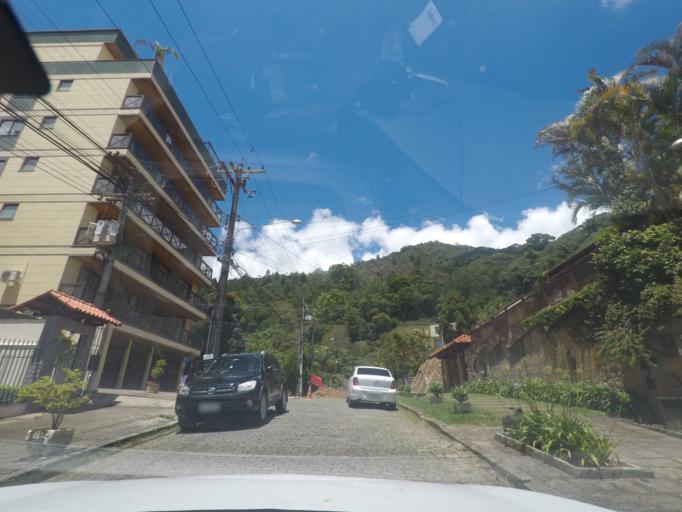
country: BR
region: Rio de Janeiro
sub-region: Teresopolis
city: Teresopolis
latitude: -22.4288
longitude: -42.9823
